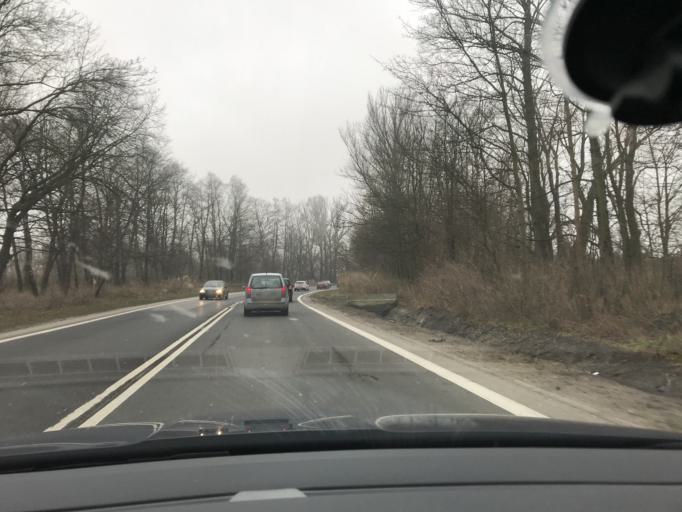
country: PL
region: Lodz Voivodeship
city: Lodz
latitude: 51.8091
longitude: 19.5016
